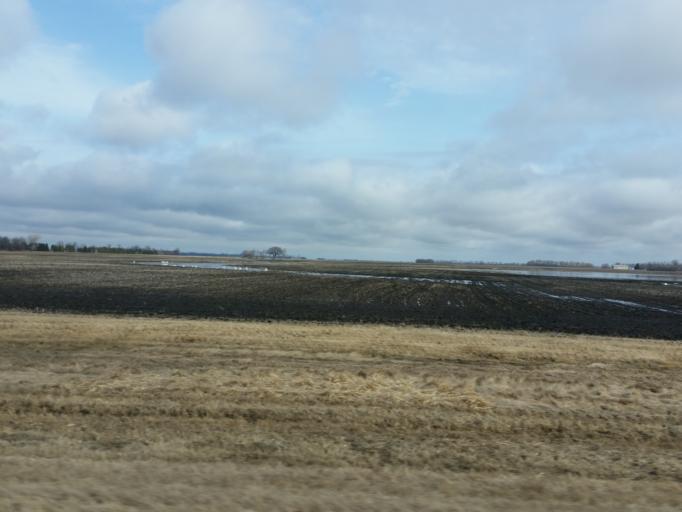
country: US
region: North Dakota
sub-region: Traill County
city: Hillsboro
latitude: 47.4978
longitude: -97.1435
